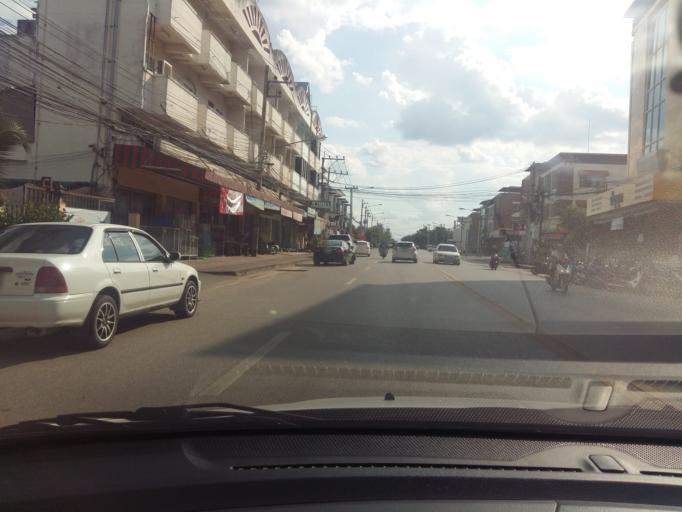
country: TH
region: Lampang
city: Lampang
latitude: 18.2690
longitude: 99.4974
